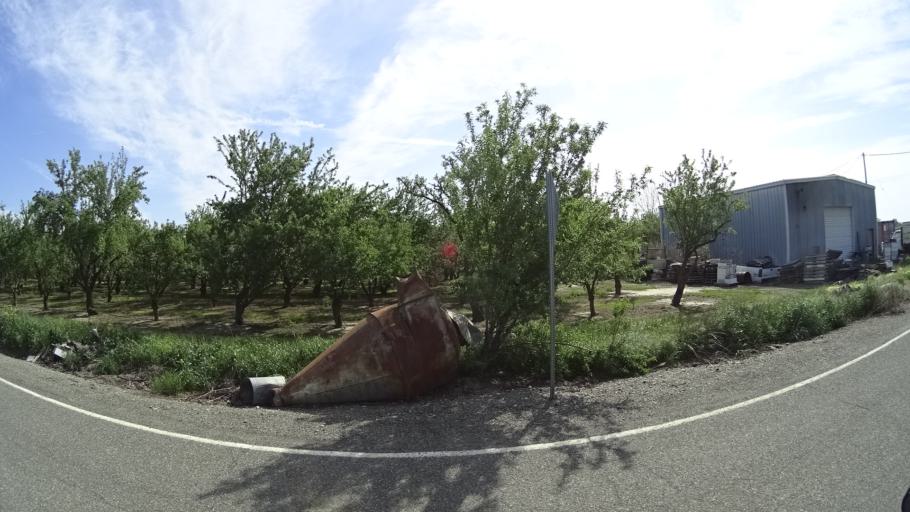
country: US
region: California
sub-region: Glenn County
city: Hamilton City
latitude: 39.6293
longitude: -122.0369
